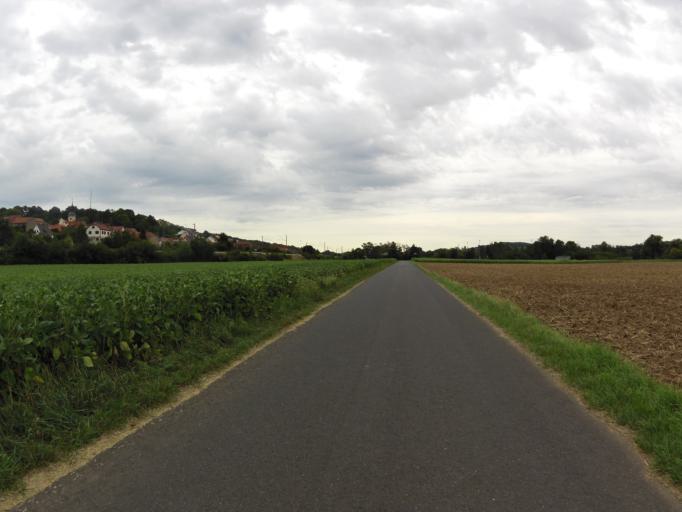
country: DE
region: Bavaria
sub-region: Regierungsbezirk Unterfranken
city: Gadheim
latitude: 50.0219
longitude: 10.3385
